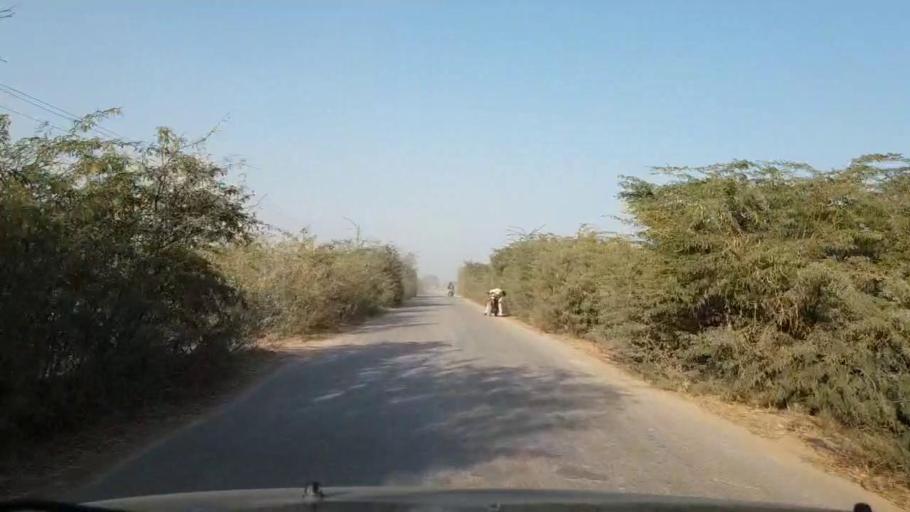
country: PK
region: Sindh
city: Chambar
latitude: 25.2595
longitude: 68.7968
